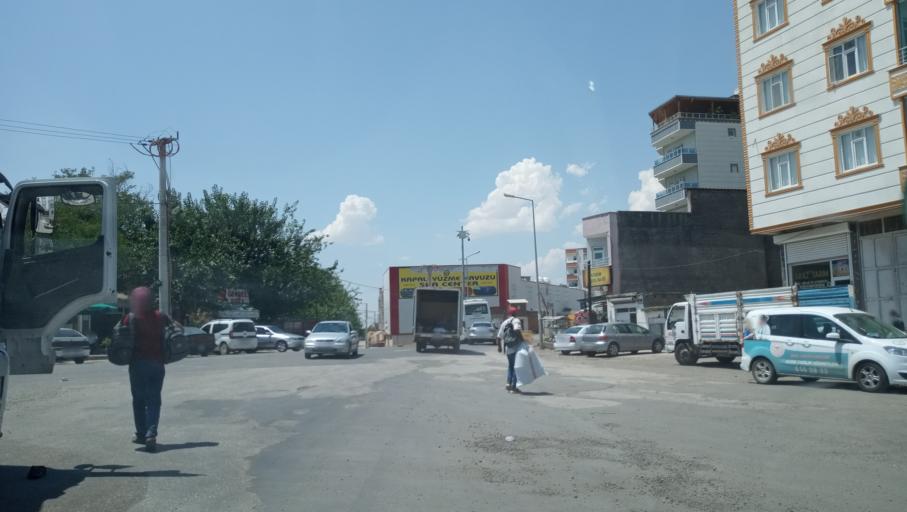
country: TR
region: Diyarbakir
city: Bismil
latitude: 37.8436
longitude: 40.6591
